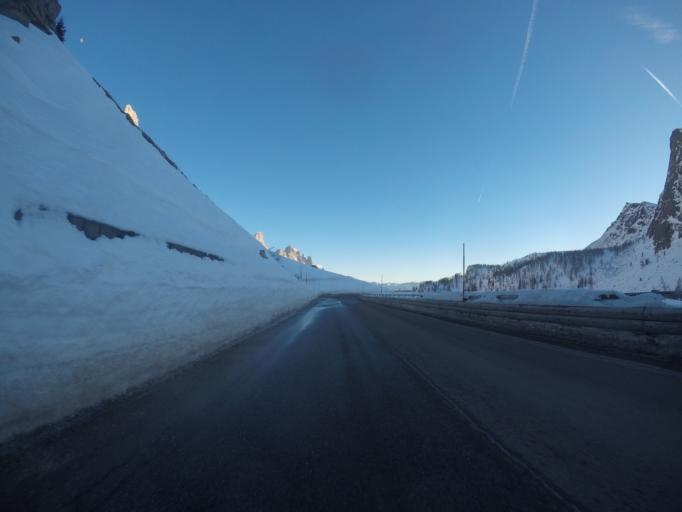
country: IT
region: Veneto
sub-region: Provincia di Belluno
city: Falcade Alto
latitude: 46.2937
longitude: 11.7937
